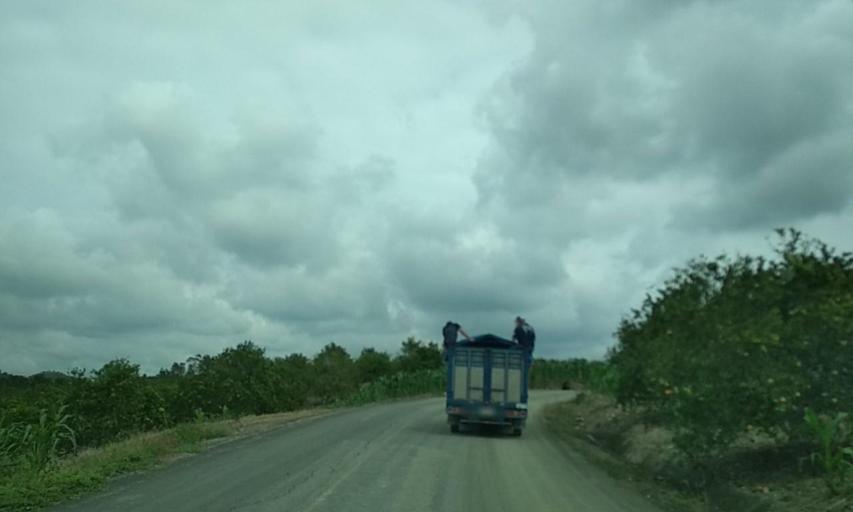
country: MX
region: Veracruz
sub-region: Papantla
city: El Chote
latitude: 20.3544
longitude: -97.3510
